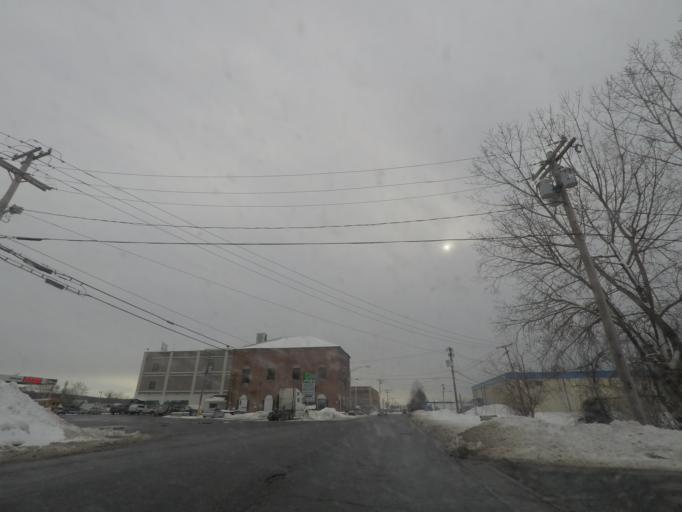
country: US
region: New York
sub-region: Rensselaer County
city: Rensselaer
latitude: 42.6356
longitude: -73.7555
